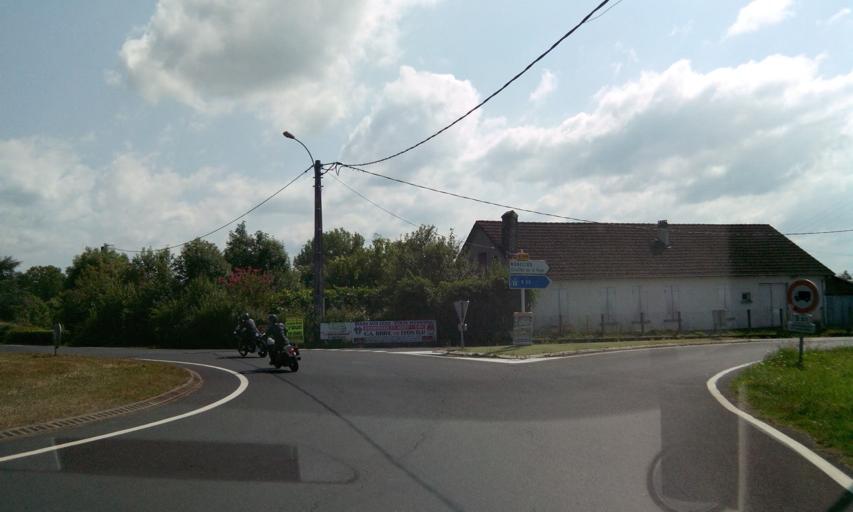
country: FR
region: Limousin
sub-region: Departement de la Correze
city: Cosnac
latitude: 45.1012
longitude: 1.5723
